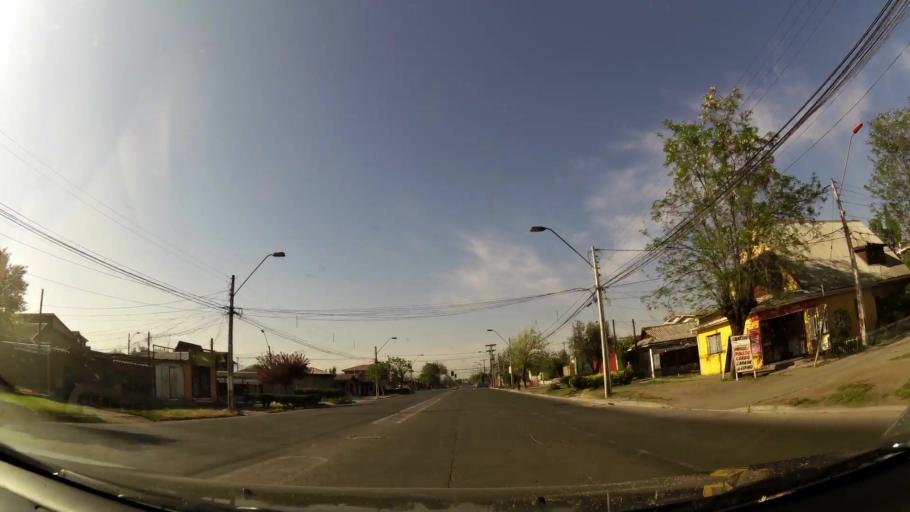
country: CL
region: Santiago Metropolitan
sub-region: Provincia de Santiago
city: Lo Prado
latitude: -33.3872
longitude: -70.6854
